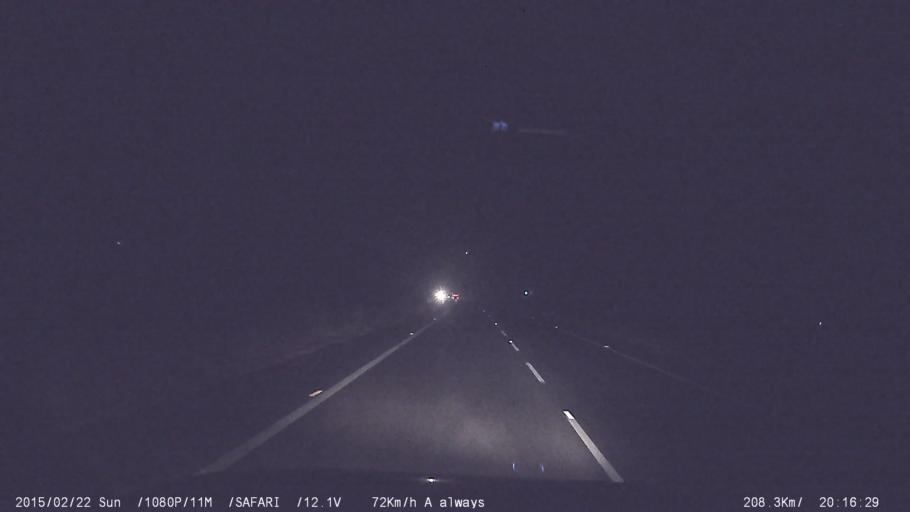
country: IN
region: Tamil Nadu
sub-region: Dindigul
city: Nilakottai
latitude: 10.2650
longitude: 77.8510
